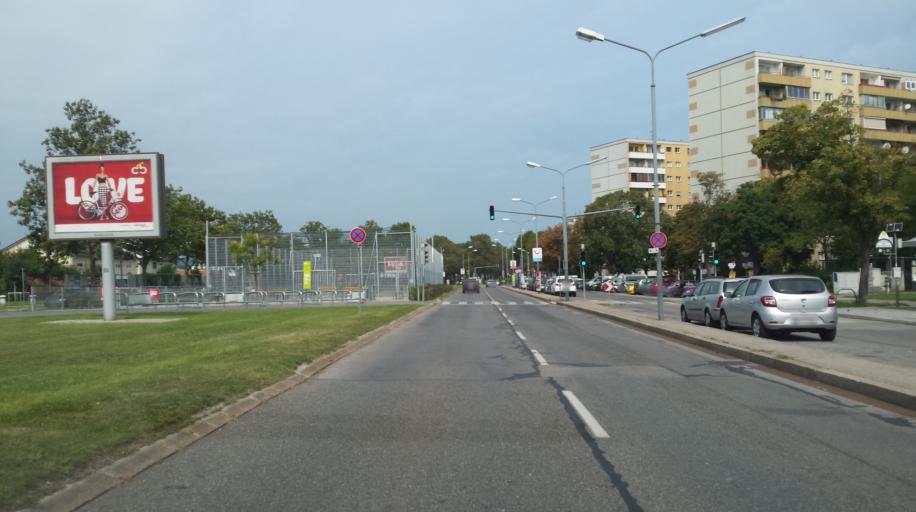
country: AT
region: Lower Austria
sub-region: Politischer Bezirk Wien-Umgebung
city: Gerasdorf bei Wien
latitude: 48.2382
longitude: 16.4399
